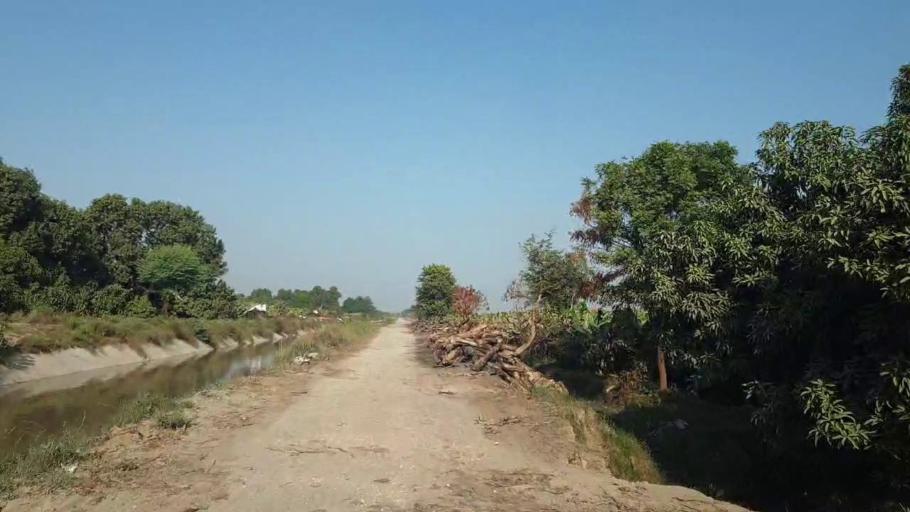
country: PK
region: Sindh
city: Matiari
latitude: 25.5340
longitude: 68.4371
